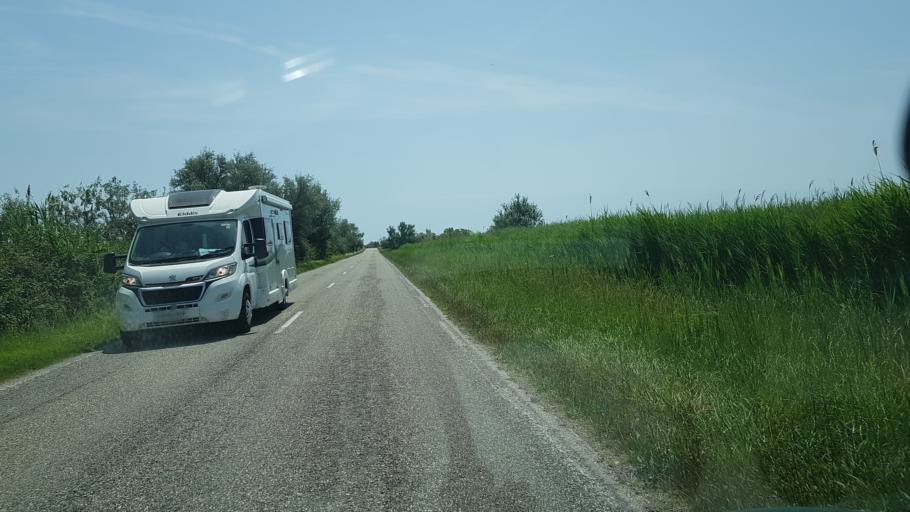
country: FR
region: Languedoc-Roussillon
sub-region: Departement du Gard
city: Saint-Gilles
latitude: 43.5757
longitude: 4.5227
